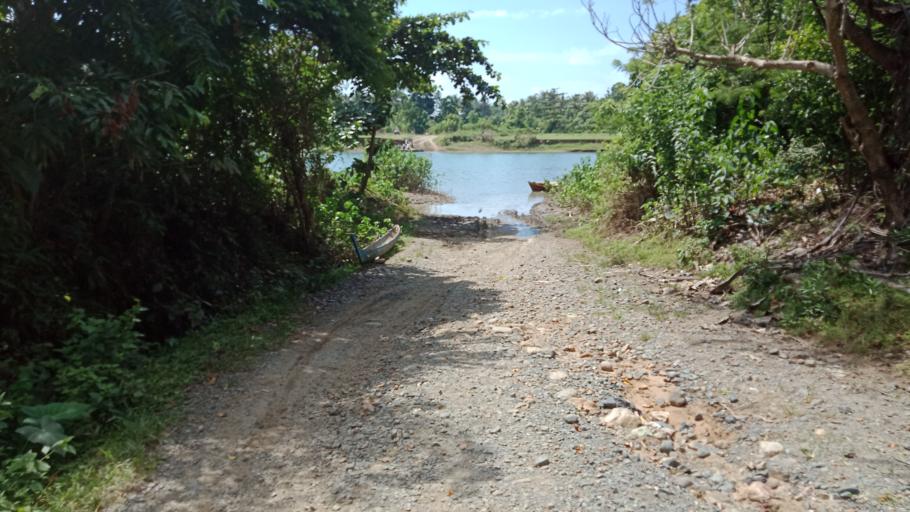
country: ID
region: South Sulawesi
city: Kadai
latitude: -4.7971
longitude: 120.3513
